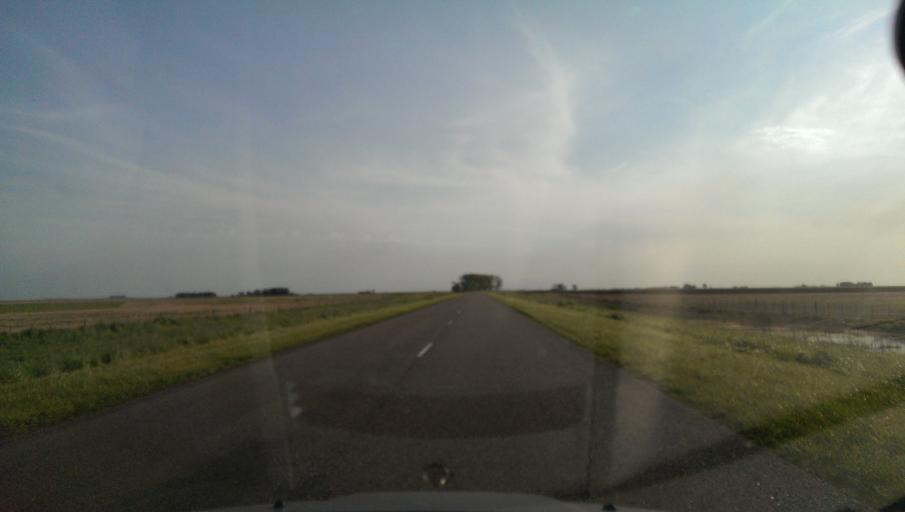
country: AR
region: Buenos Aires
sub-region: Partido de General La Madrid
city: General La Madrid
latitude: -37.5533
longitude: -61.2744
